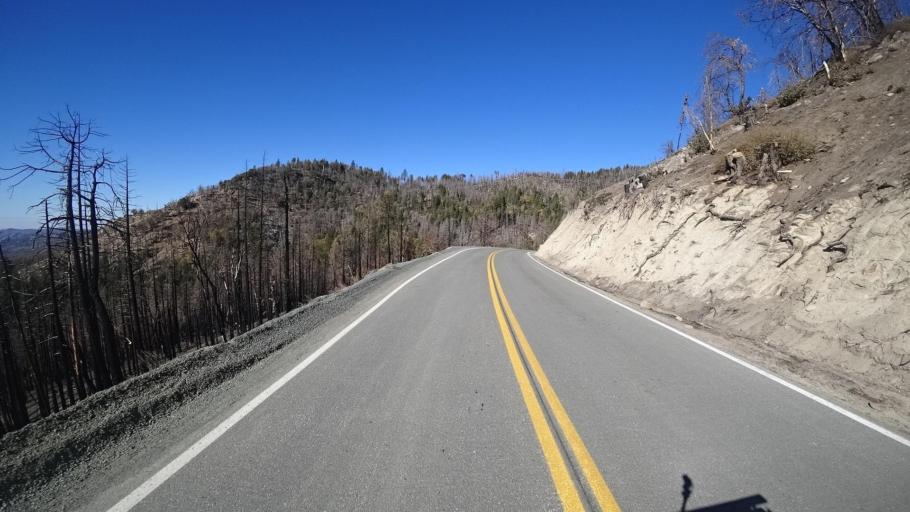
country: US
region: California
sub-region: Kern County
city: Alta Sierra
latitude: 35.7477
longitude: -118.5574
